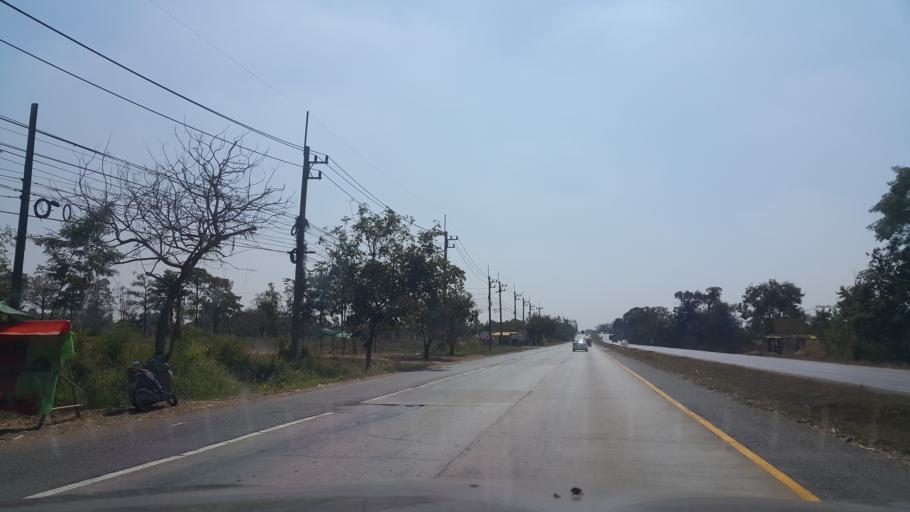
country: TH
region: Khon Kaen
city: Nam Phong
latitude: 16.8182
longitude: 102.8377
